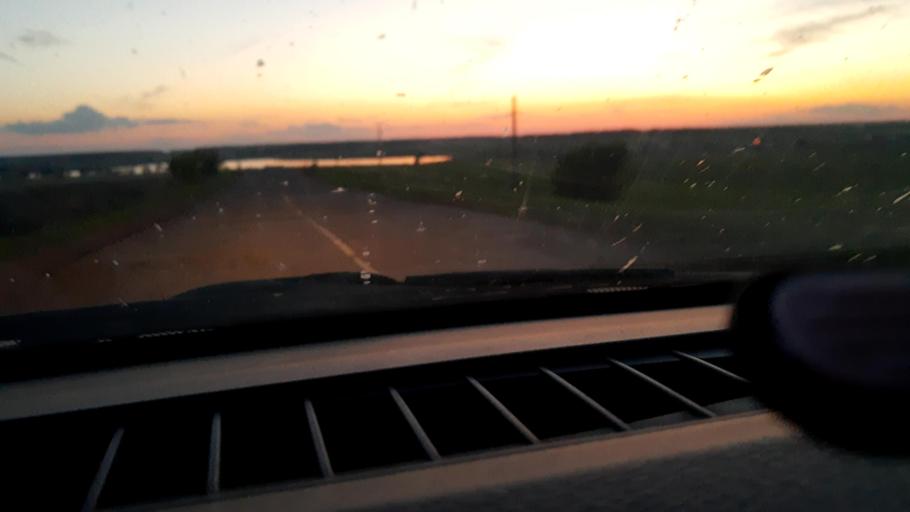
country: RU
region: Bashkortostan
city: Asanovo
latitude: 54.8469
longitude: 55.6032
